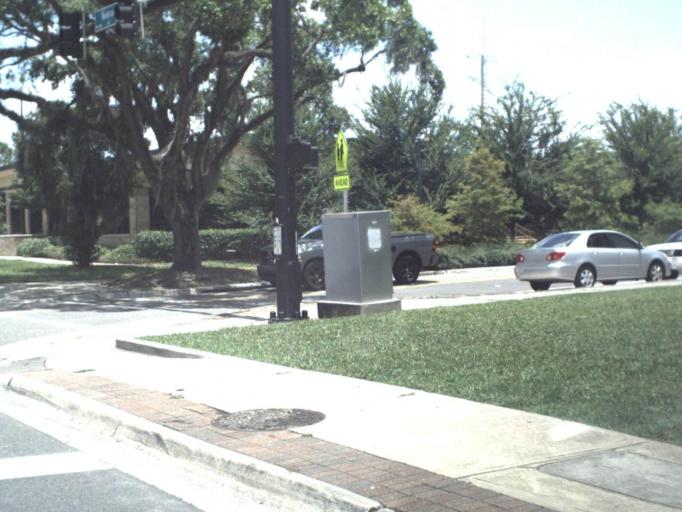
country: US
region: Florida
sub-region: Duval County
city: Jacksonville
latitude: 30.3086
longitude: -81.6547
